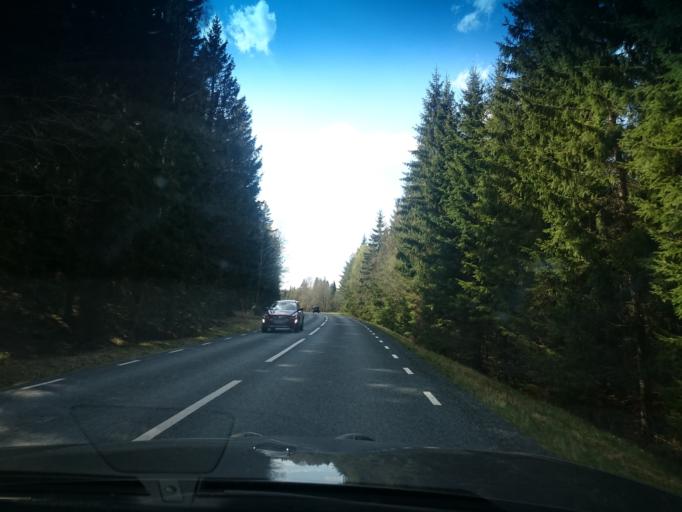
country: SE
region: Joenkoeping
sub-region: Vetlanda Kommun
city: Vetlanda
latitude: 57.3650
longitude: 15.2560
